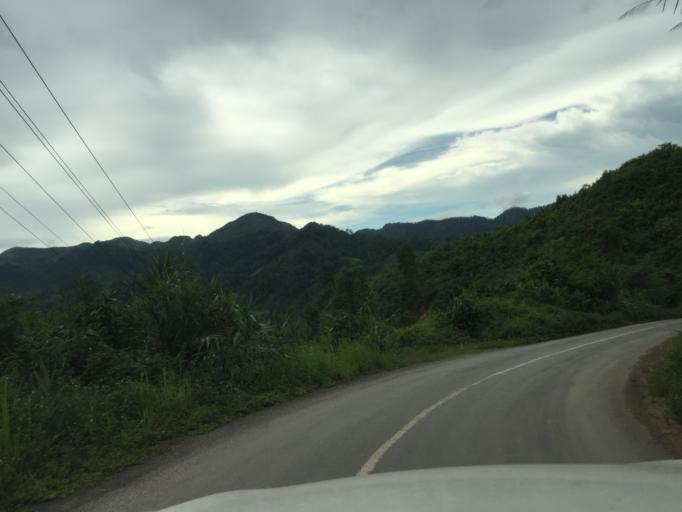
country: LA
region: Oudomxai
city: Muang La
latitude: 21.2364
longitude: 102.0754
